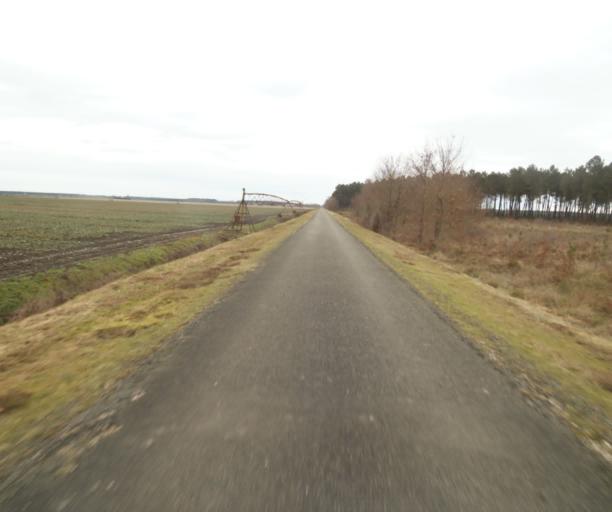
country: FR
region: Aquitaine
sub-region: Departement des Landes
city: Gabarret
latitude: 44.0298
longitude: -0.0596
